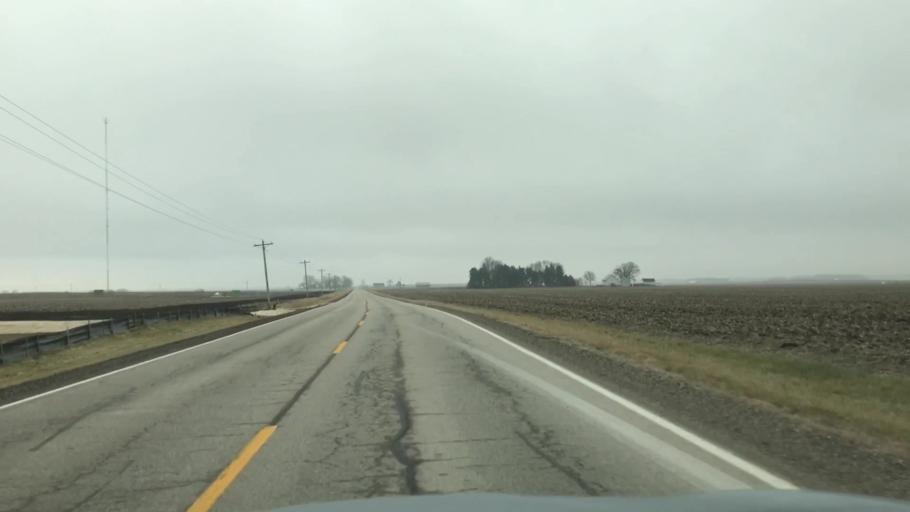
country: US
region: Illinois
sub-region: McLean County
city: Hudson
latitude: 40.5832
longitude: -88.9448
